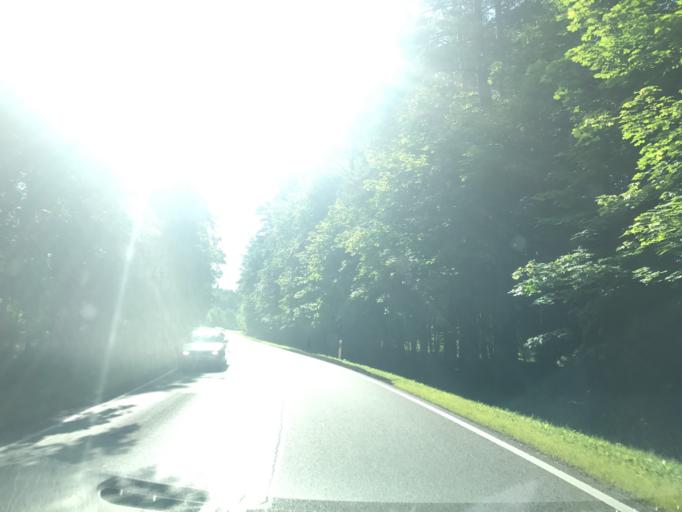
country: PL
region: Pomeranian Voivodeship
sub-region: Powiat czluchowski
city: Czluchow
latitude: 53.7030
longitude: 17.2710
